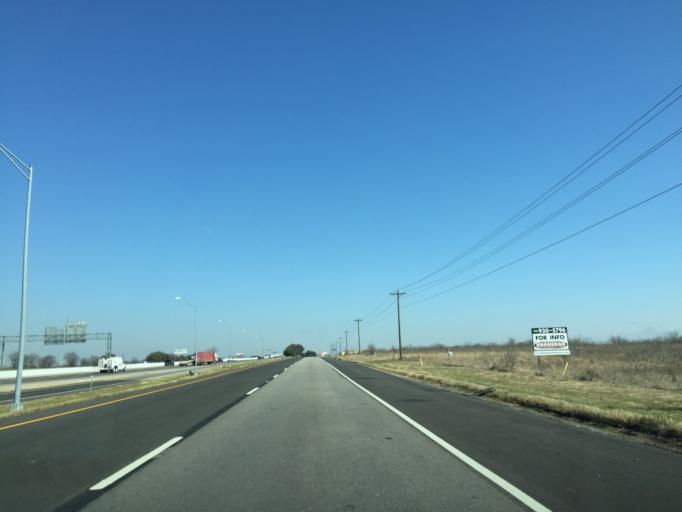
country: US
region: Texas
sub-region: Williamson County
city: Serenada
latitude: 30.7158
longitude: -97.6463
